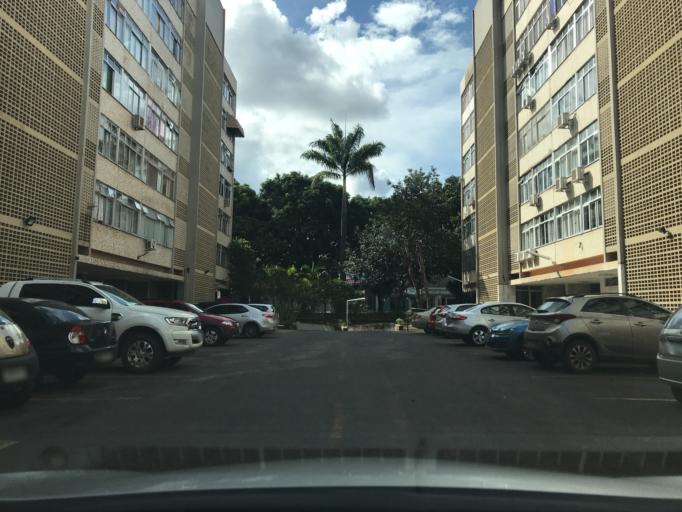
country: BR
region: Federal District
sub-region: Brasilia
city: Brasilia
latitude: -15.8020
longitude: -47.8929
